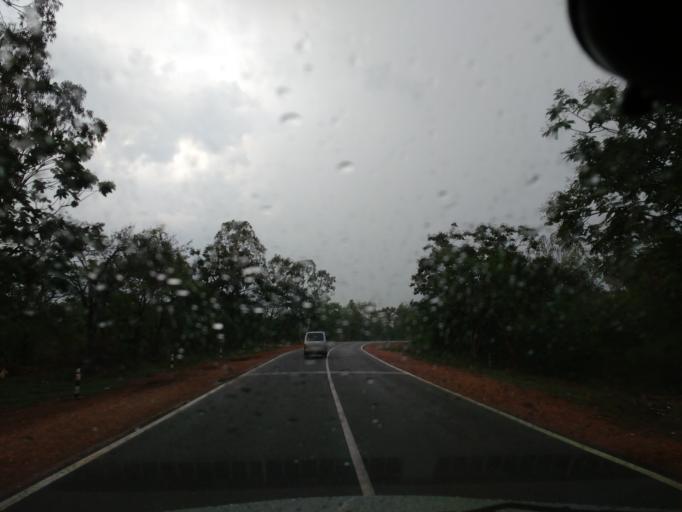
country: IN
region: Karnataka
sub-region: Tumkur
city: Tiptur
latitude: 13.2967
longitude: 76.5848
